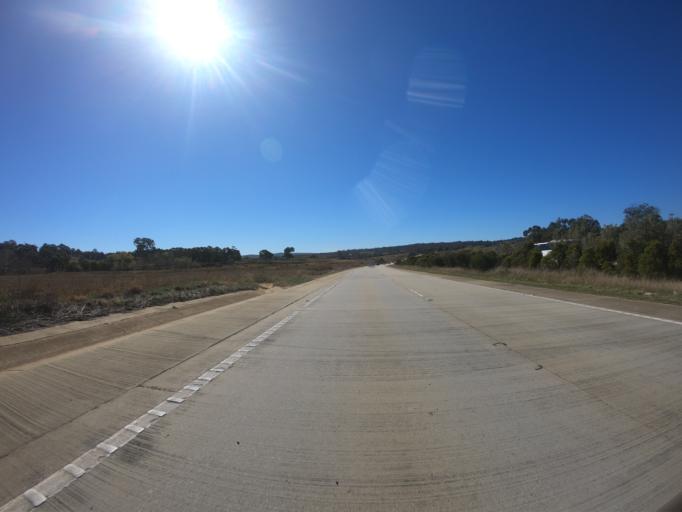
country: AU
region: New South Wales
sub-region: Yass Valley
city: Gundaroo
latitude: -35.1228
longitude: 149.3446
